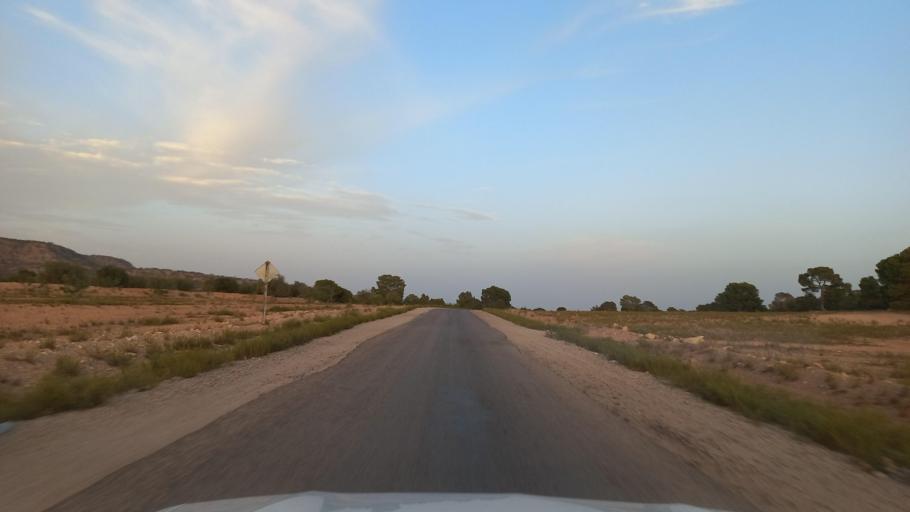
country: TN
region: Al Qasrayn
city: Sbiba
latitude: 35.4138
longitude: 8.9297
